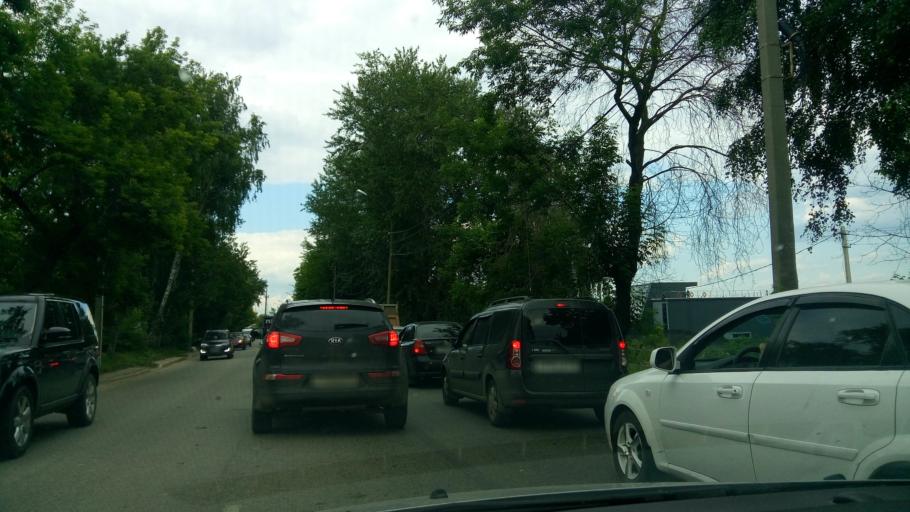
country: RU
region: Sverdlovsk
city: Yekaterinburg
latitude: 56.8732
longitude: 60.6872
